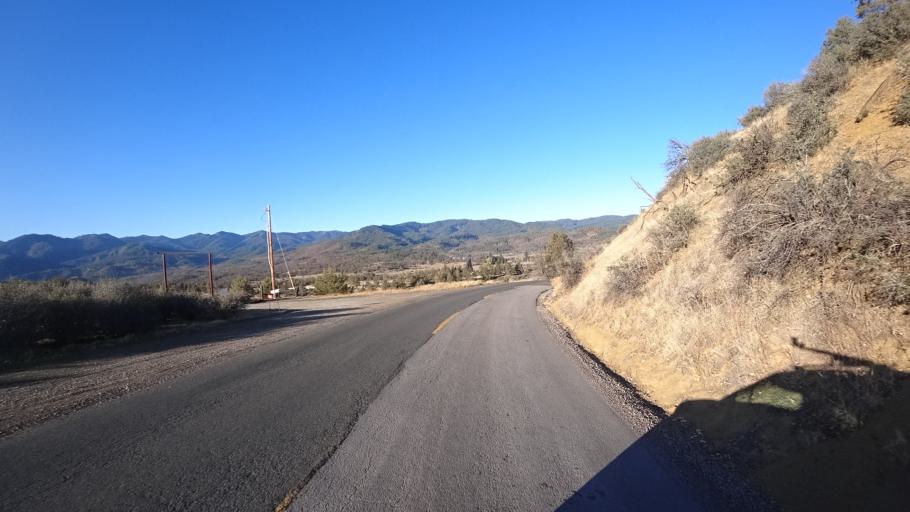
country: US
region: Oregon
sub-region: Jackson County
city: Ashland
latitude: 41.9954
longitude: -122.6150
